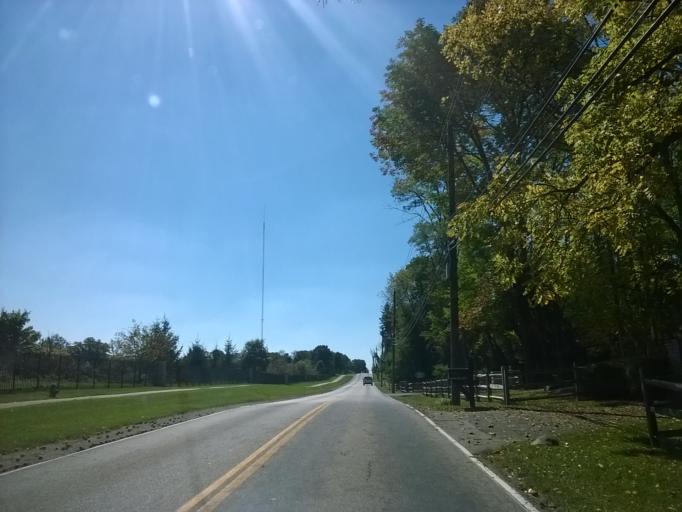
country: US
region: Indiana
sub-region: Marion County
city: Meridian Hills
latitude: 39.9380
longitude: -86.1841
